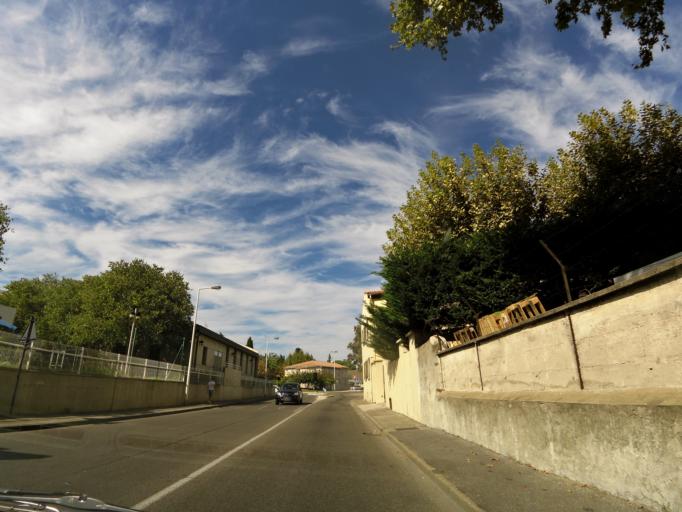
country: FR
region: Languedoc-Roussillon
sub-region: Departement du Gard
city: Nimes
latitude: 43.8245
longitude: 4.3628
